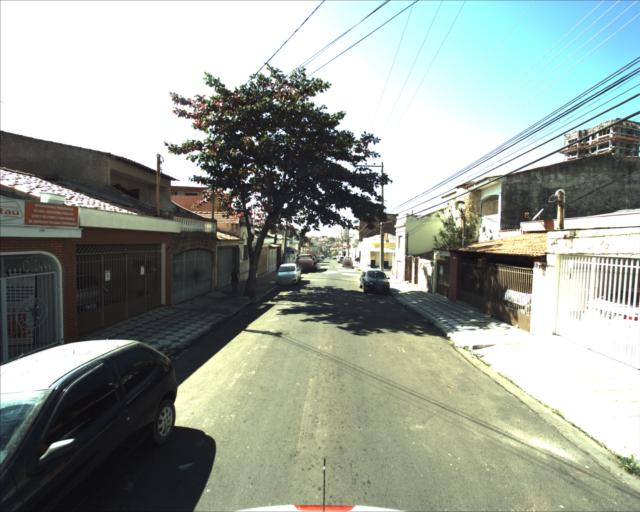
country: BR
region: Sao Paulo
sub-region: Sorocaba
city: Sorocaba
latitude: -23.5049
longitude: -47.4450
